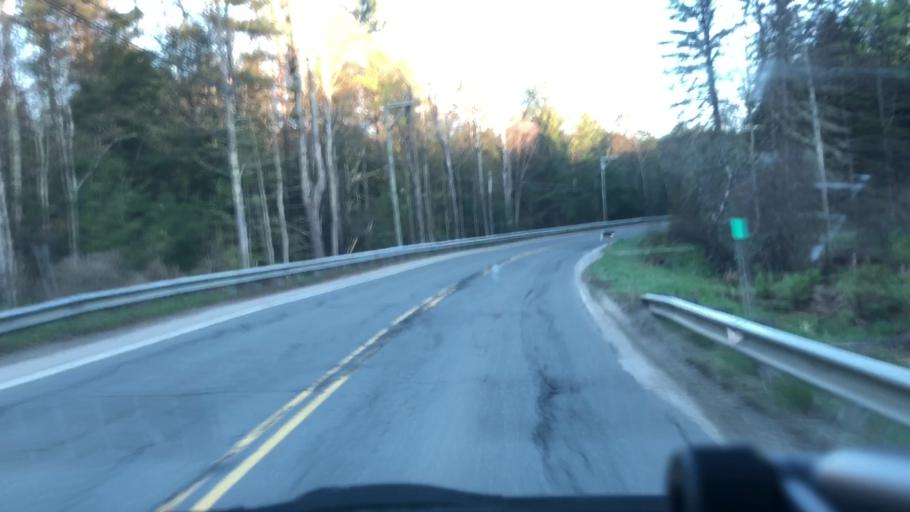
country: US
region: Massachusetts
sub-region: Hampshire County
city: Westhampton
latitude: 42.2831
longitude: -72.8316
